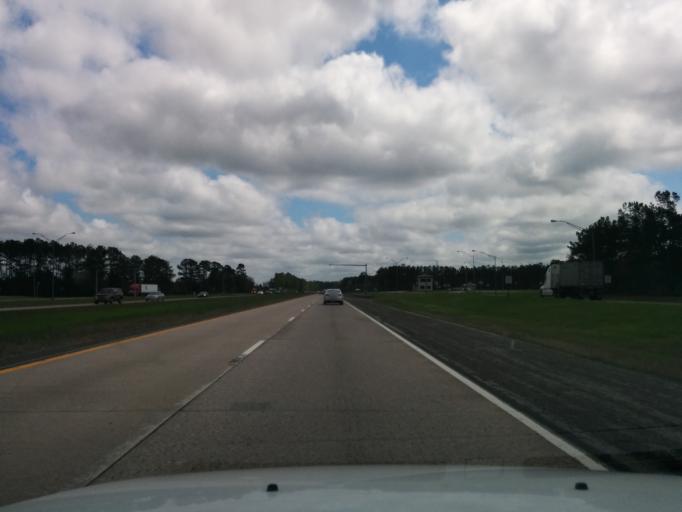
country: US
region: Georgia
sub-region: Chatham County
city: Bloomingdale
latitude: 32.1698
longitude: -81.4453
